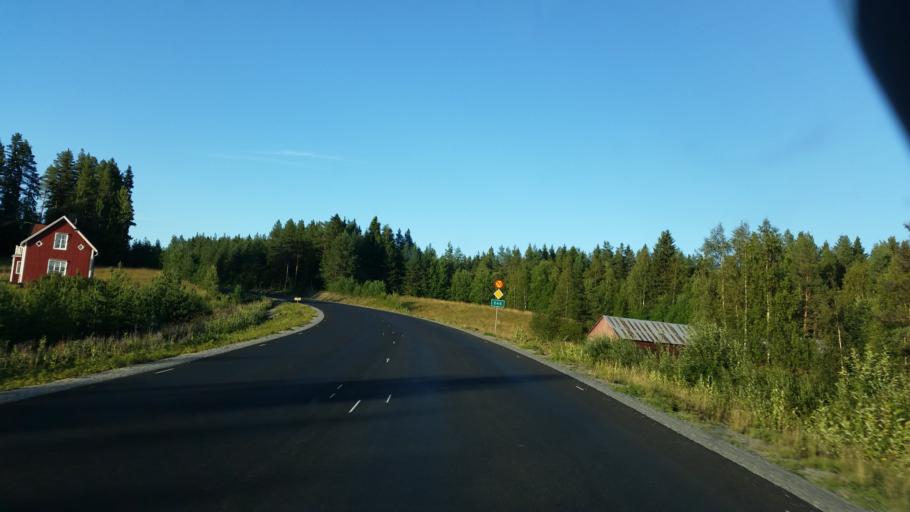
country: SE
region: Vaesterbotten
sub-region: Dorotea Kommun
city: Dorotea
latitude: 64.2532
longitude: 16.4778
